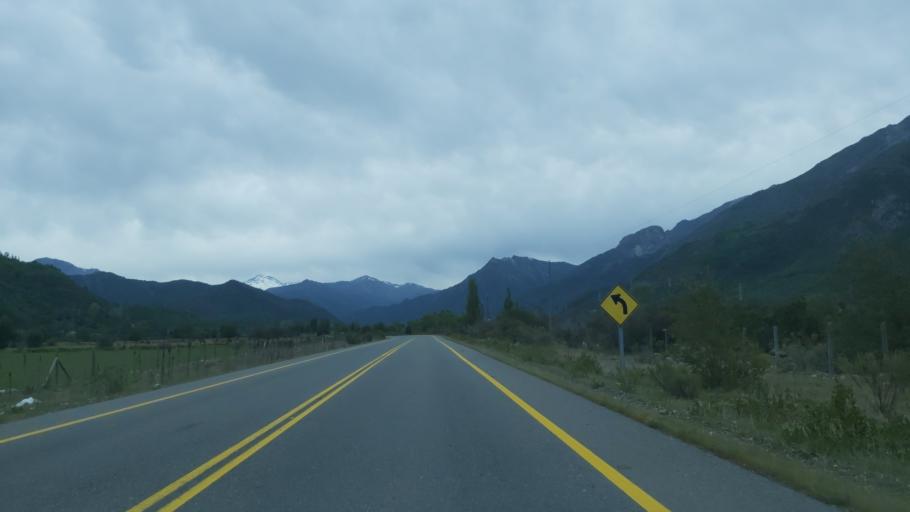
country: CL
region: Maule
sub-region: Provincia de Linares
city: Colbun
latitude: -35.7364
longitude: -71.0114
